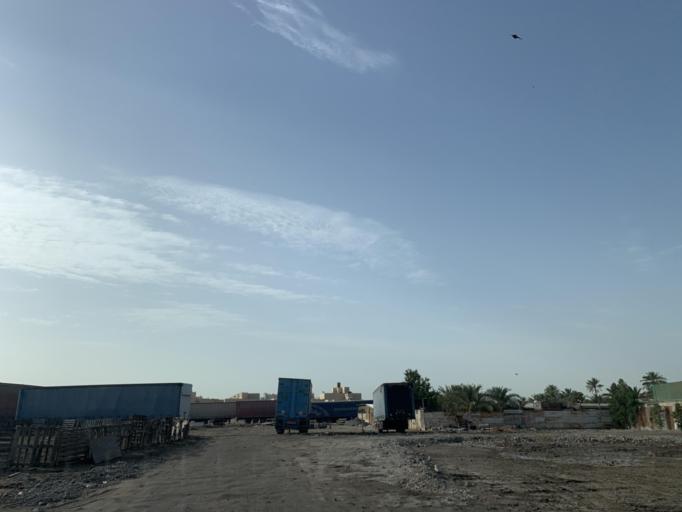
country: BH
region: Manama
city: Manama
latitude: 26.1817
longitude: 50.5873
